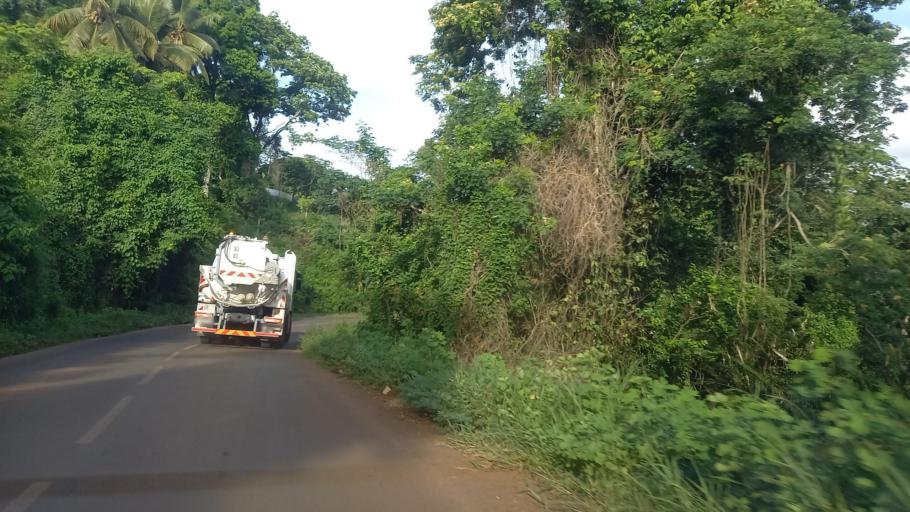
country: YT
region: Chiconi
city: Chiconi
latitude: -12.8209
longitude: 45.1307
